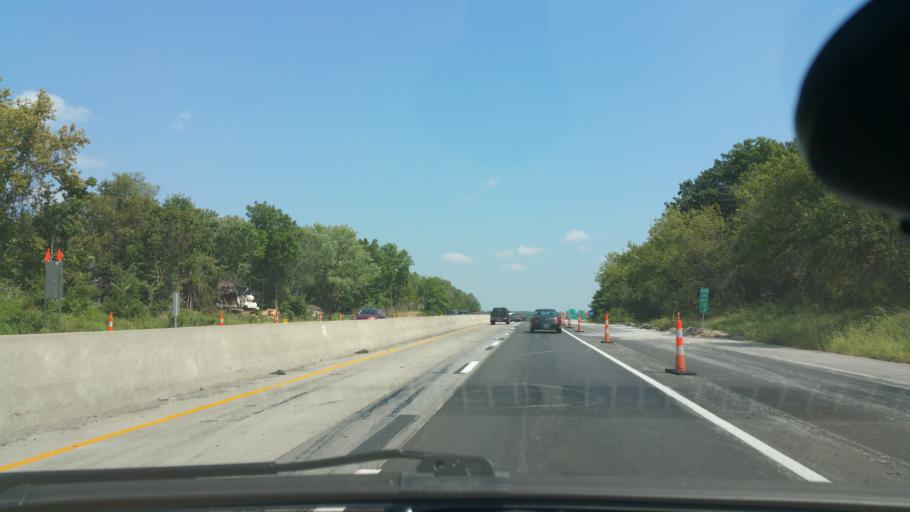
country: US
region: Missouri
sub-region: Clay County
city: Claycomo
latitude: 39.2038
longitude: -94.5007
